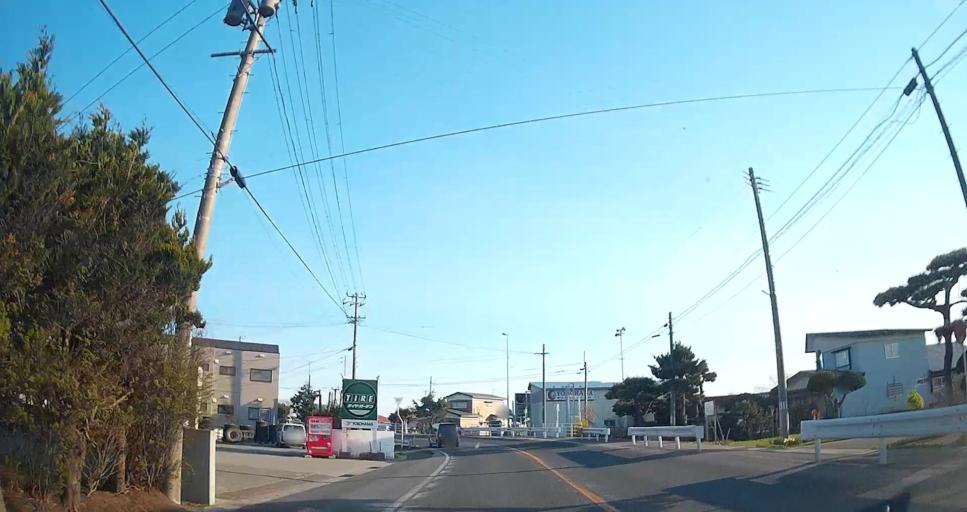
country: JP
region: Aomori
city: Mutsu
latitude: 41.2804
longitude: 141.2095
